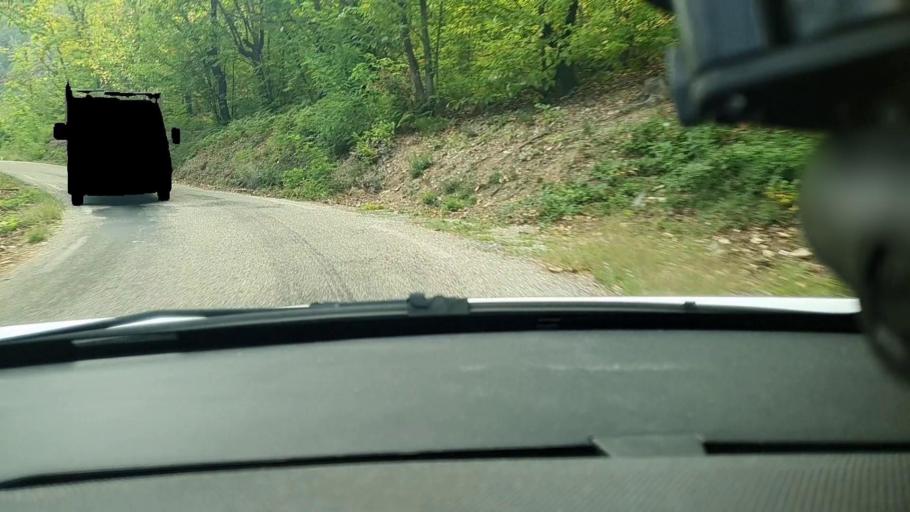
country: FR
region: Languedoc-Roussillon
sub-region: Departement du Gard
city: Branoux-les-Taillades
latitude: 44.2213
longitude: 3.9795
